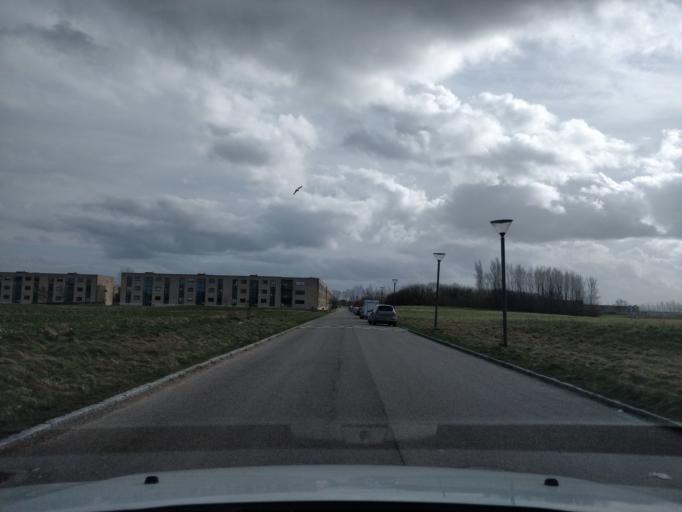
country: DK
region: Capital Region
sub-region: Hoje-Taastrup Kommune
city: Taastrup
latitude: 55.6454
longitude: 12.2619
